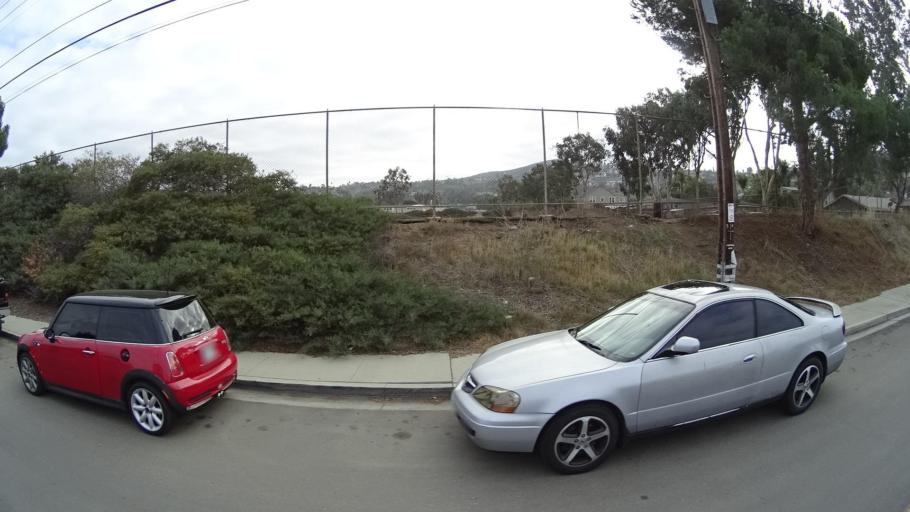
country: US
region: California
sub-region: San Diego County
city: Spring Valley
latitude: 32.7293
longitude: -117.0101
